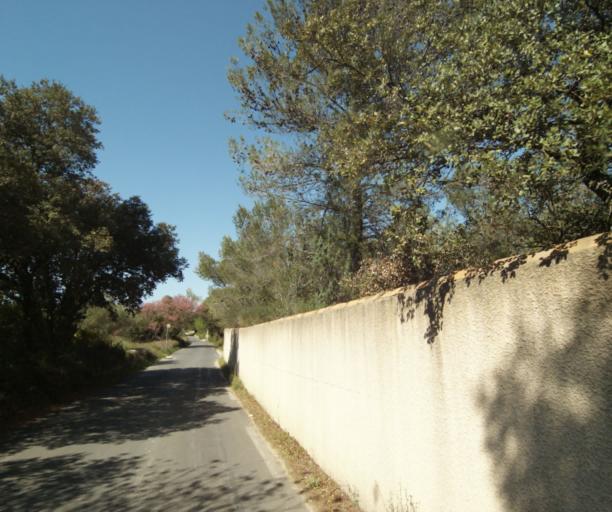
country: FR
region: Languedoc-Roussillon
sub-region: Departement de l'Herault
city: Sussargues
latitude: 43.6921
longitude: 3.9990
